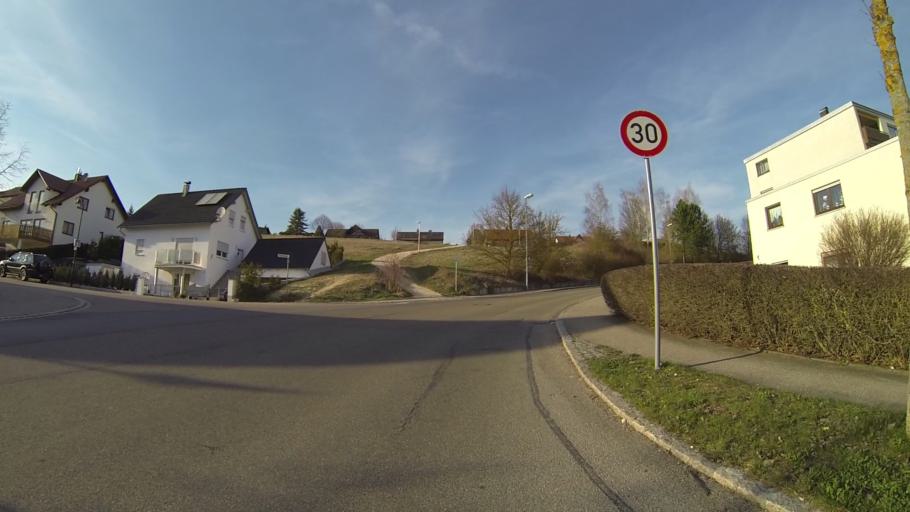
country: DE
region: Baden-Wuerttemberg
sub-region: Regierungsbezirk Stuttgart
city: Herbrechtingen
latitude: 48.6321
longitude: 10.1777
